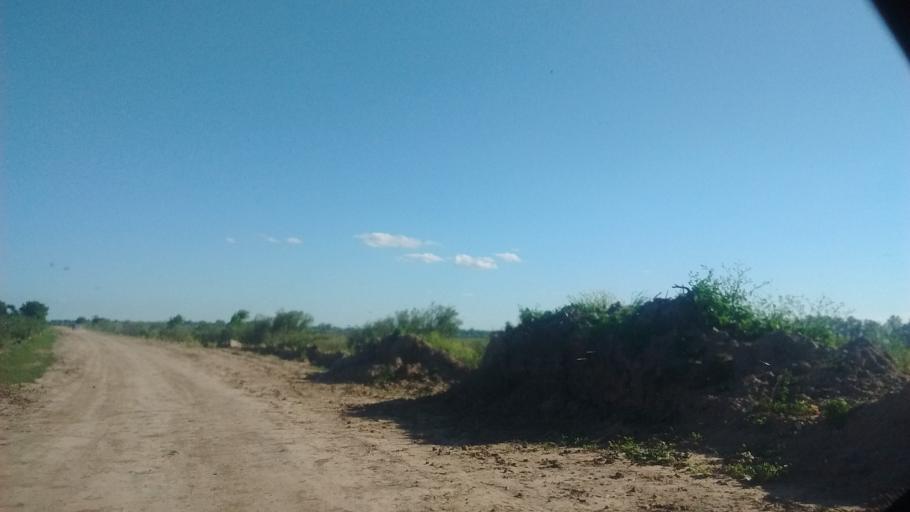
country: AR
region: Santa Fe
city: Funes
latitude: -32.8867
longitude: -60.7979
